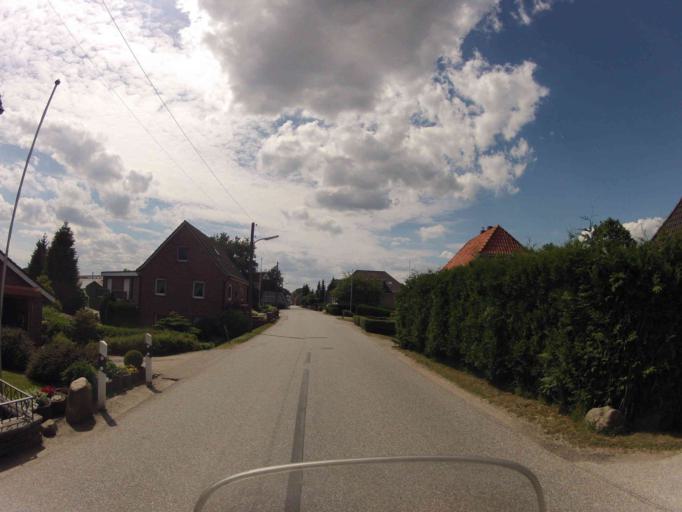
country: DE
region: Hamburg
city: Bergedorf
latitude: 53.4436
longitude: 10.1795
